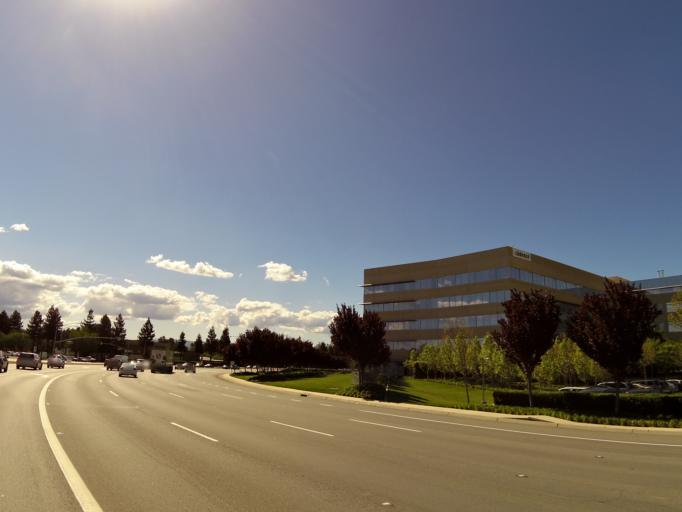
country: US
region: California
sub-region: Santa Clara County
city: Milpitas
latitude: 37.3941
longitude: -121.9176
